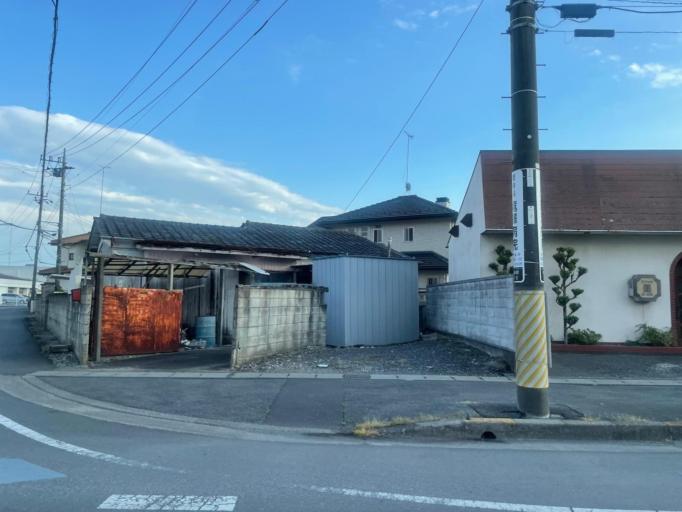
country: JP
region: Tochigi
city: Tochigi
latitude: 36.3726
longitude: 139.7244
